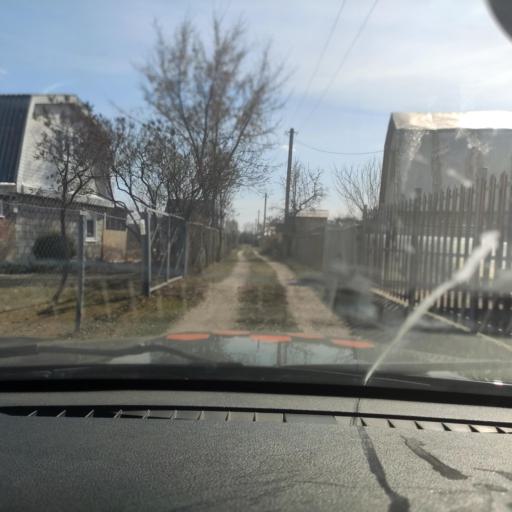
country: RU
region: Samara
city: Tol'yatti
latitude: 53.7046
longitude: 49.4120
